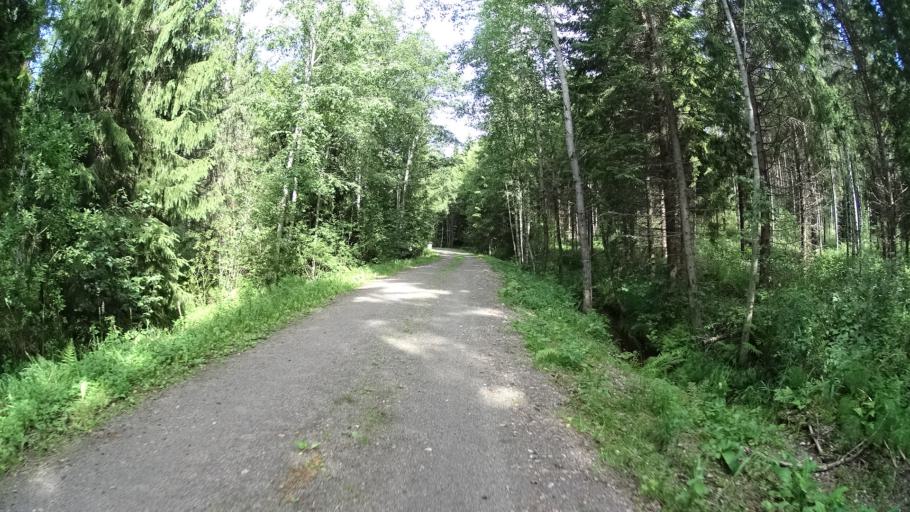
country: FI
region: Uusimaa
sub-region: Helsinki
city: Espoo
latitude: 60.2414
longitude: 24.6232
